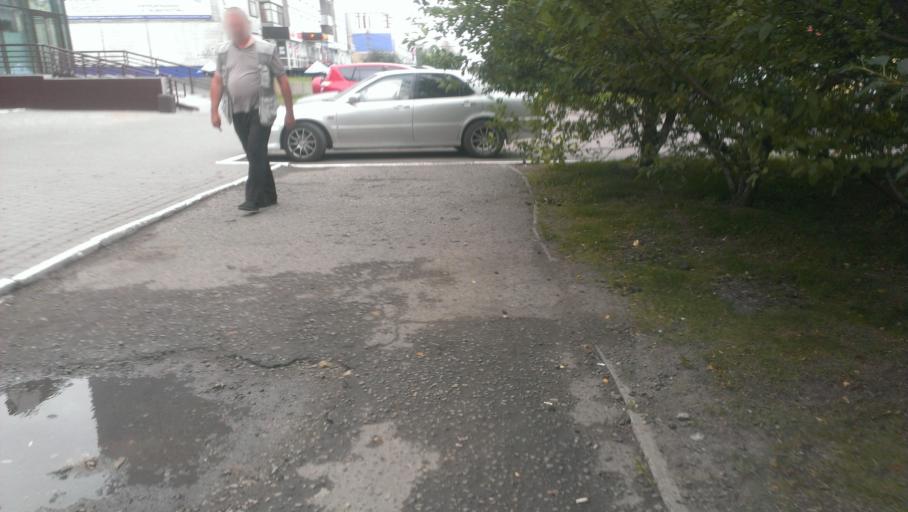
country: RU
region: Altai Krai
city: Novosilikatnyy
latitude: 53.3358
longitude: 83.6739
